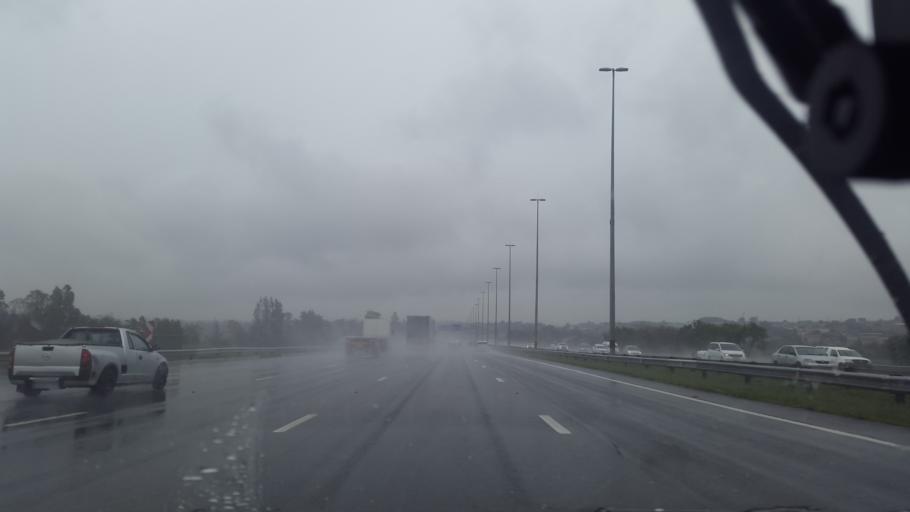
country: ZA
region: Gauteng
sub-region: City of Johannesburg Metropolitan Municipality
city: Roodepoort
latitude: -26.1972
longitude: 27.9518
